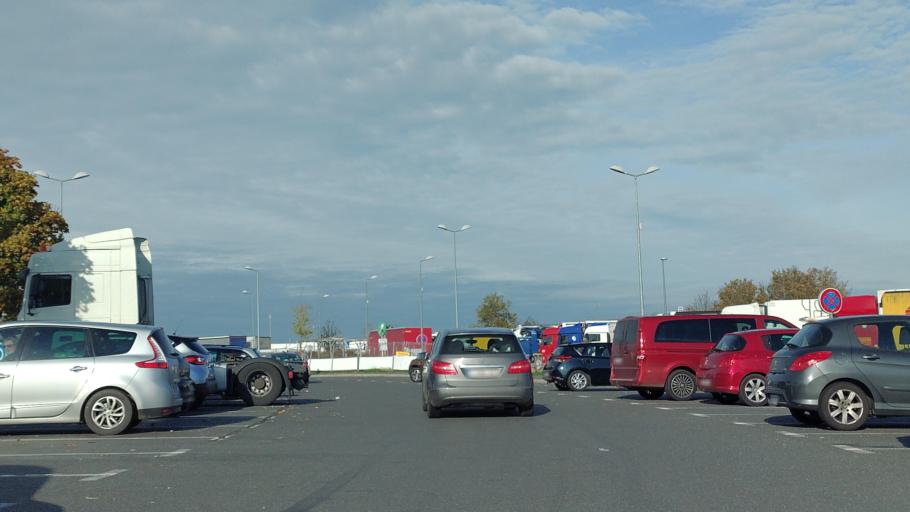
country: FR
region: Ile-de-France
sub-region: Departement du Val-d'Oise
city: Vemars
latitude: 49.0717
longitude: 2.5530
